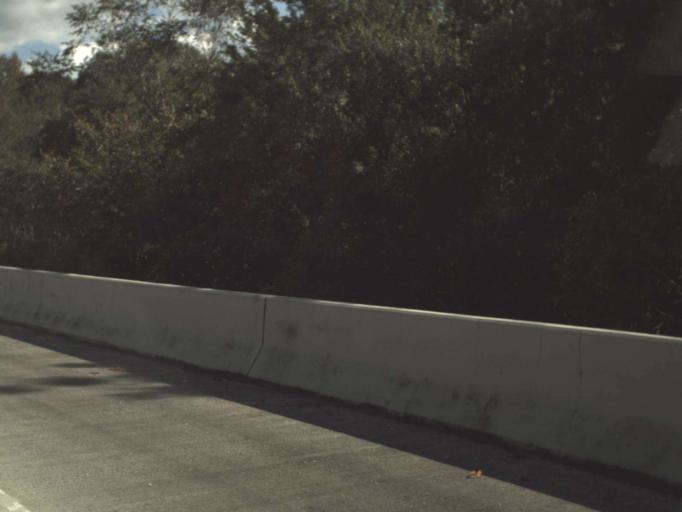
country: US
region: Florida
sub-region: Bay County
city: Laguna Beach
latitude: 30.4492
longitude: -85.8926
